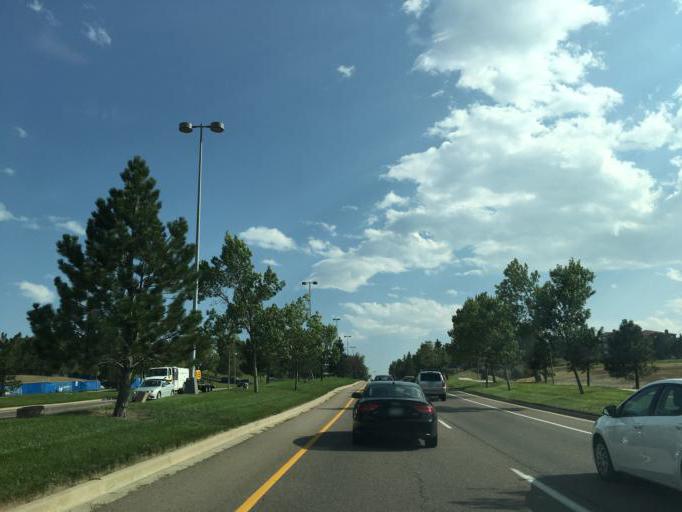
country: US
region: Colorado
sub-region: Broomfield County
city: Broomfield
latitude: 39.9278
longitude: -105.1279
